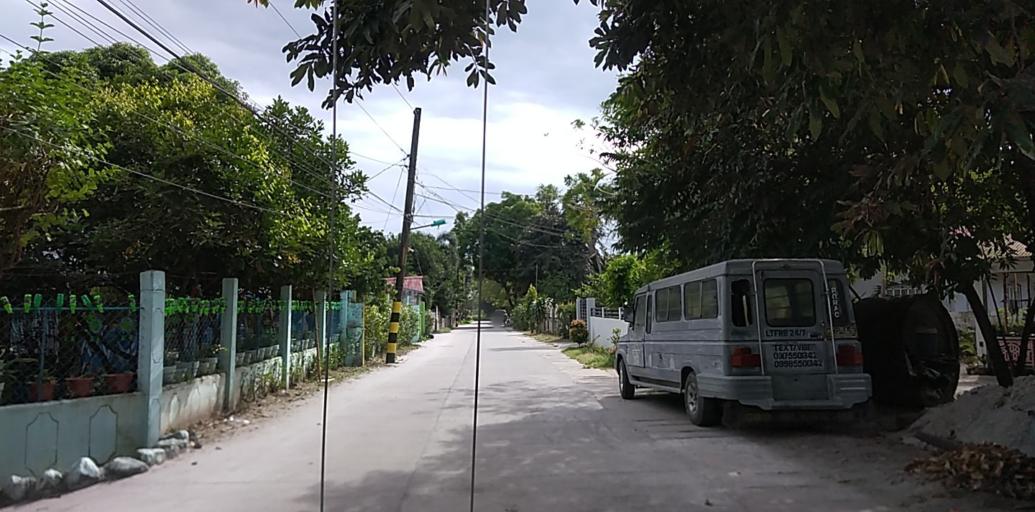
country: PH
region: Central Luzon
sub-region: Province of Pampanga
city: Pulung Santol
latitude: 15.0458
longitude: 120.5557
